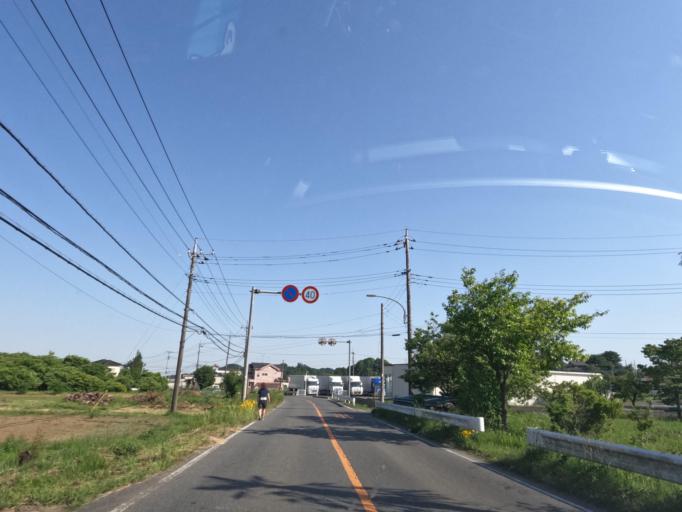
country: JP
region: Saitama
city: Ogawa
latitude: 36.0701
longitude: 139.2976
